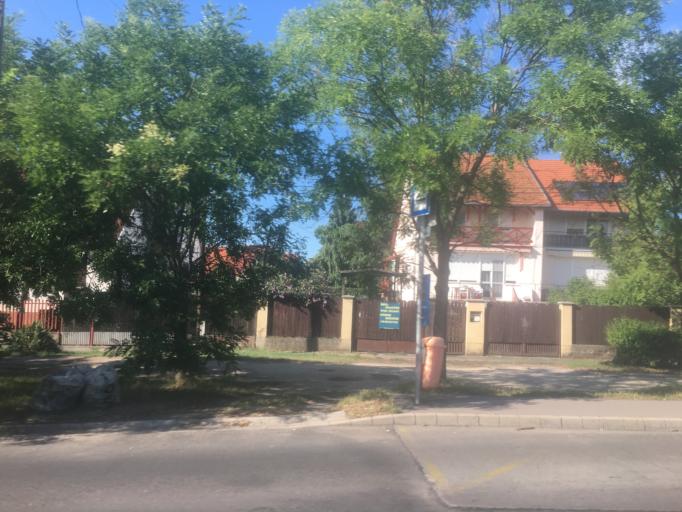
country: HU
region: Budapest
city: Budapest XVII. keruelet
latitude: 47.4738
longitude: 19.2729
